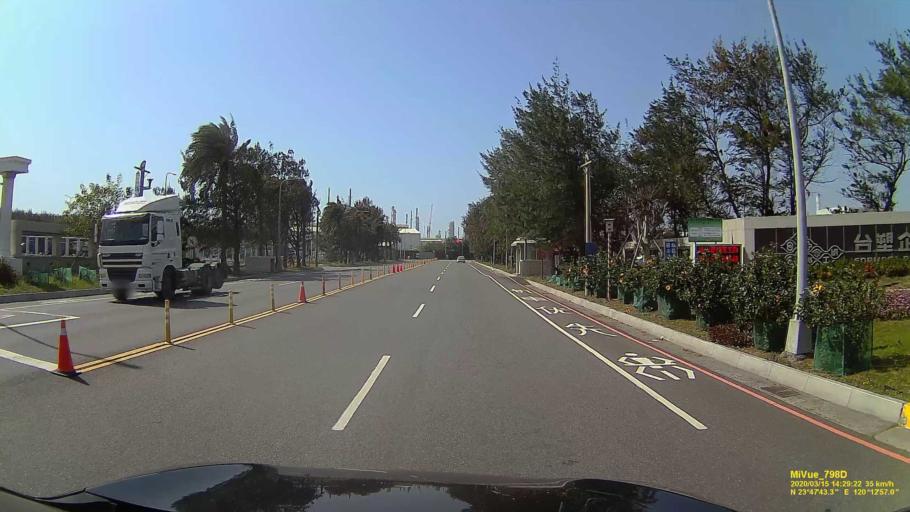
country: TW
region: Taiwan
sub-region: Yunlin
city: Douliu
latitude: 23.7954
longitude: 120.2159
